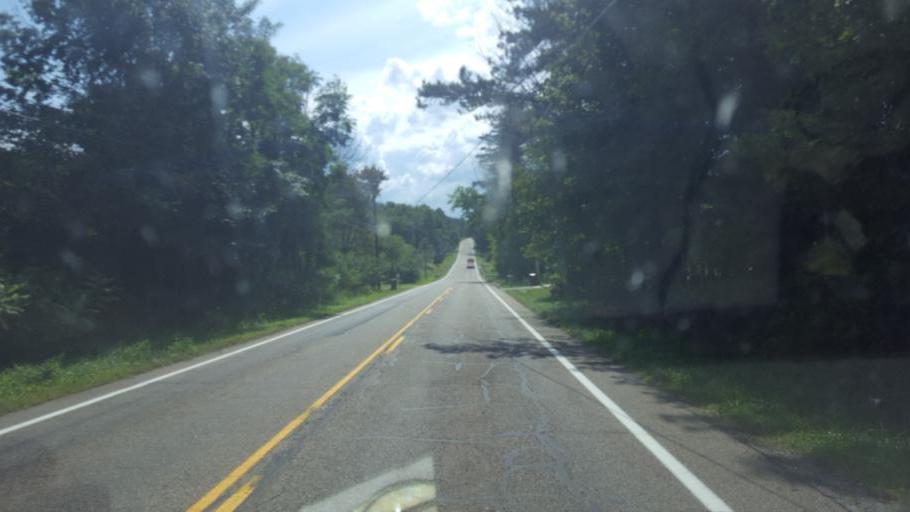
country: US
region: Ohio
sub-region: Portage County
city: Mantua
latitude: 41.2218
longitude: -81.1639
